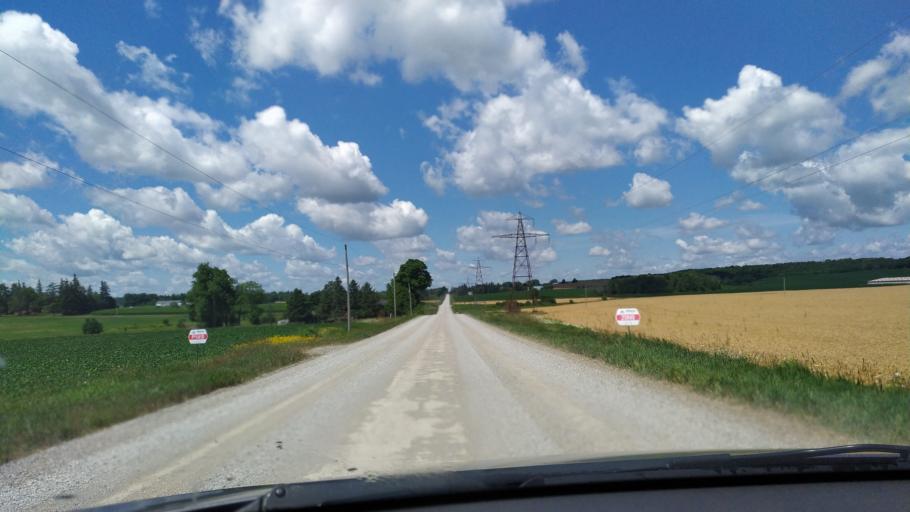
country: CA
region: Ontario
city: Stratford
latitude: 43.3874
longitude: -80.7643
